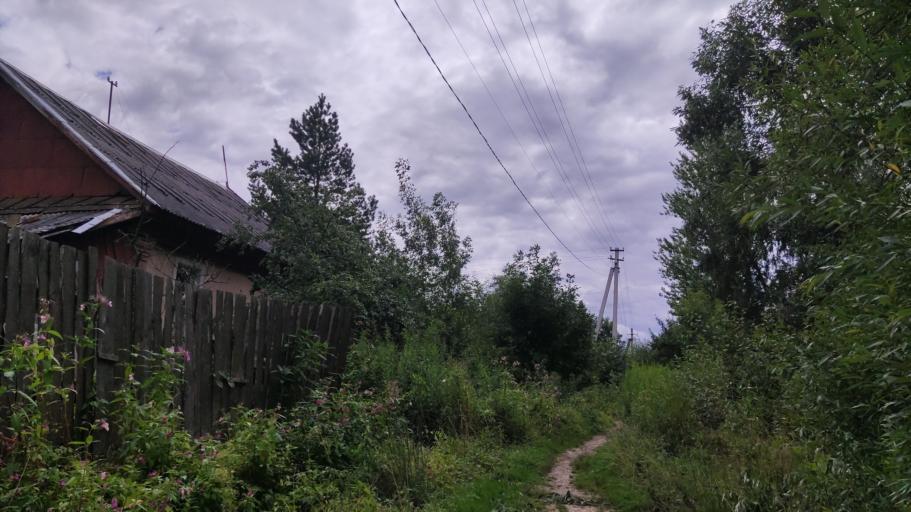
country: RU
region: Tverskaya
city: Rzhev
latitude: 56.2470
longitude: 34.3069
